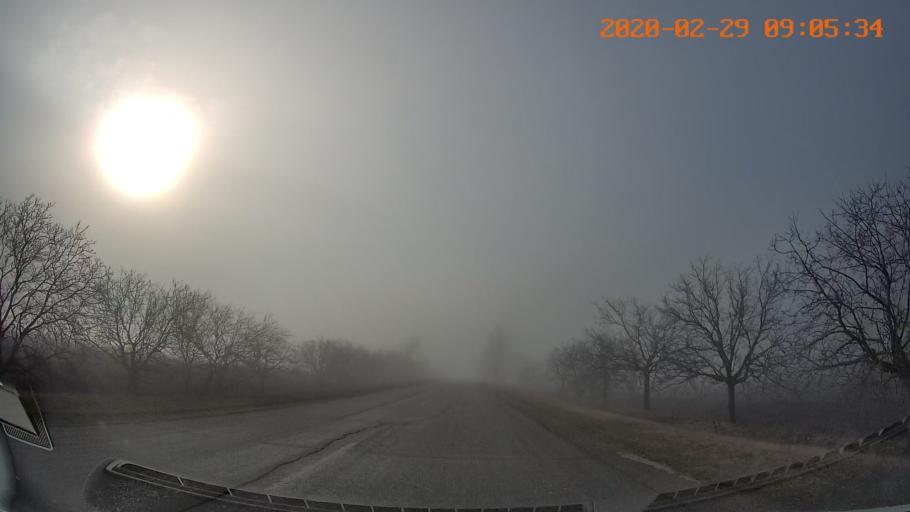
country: MD
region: Telenesti
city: Tiraspolul Nou
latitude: 46.8875
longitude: 29.7408
